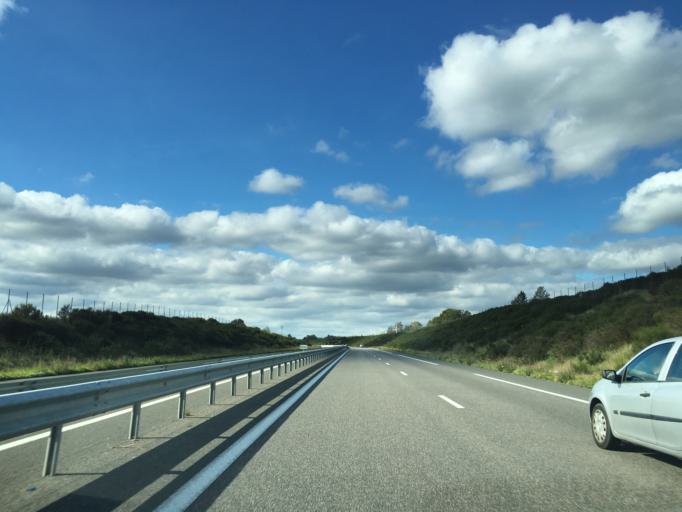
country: FR
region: Lorraine
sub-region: Departement de Meurthe-et-Moselle
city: Baccarat
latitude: 48.5229
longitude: 6.6405
